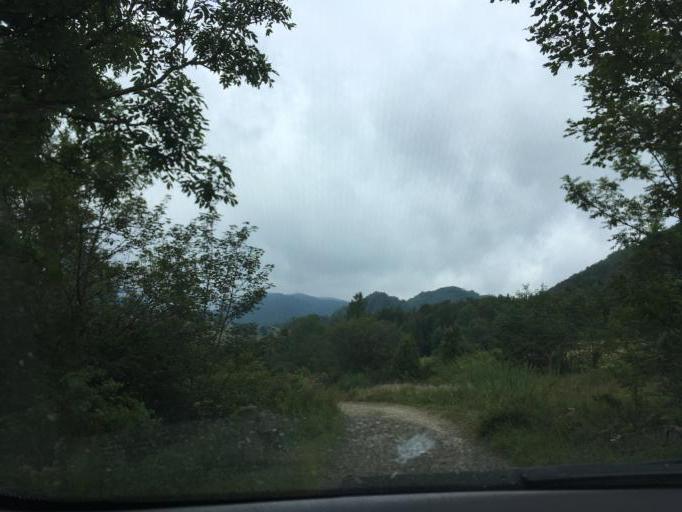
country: PL
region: Subcarpathian Voivodeship
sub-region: Powiat bieszczadzki
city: Lutowiska
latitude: 49.1648
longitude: 22.6220
